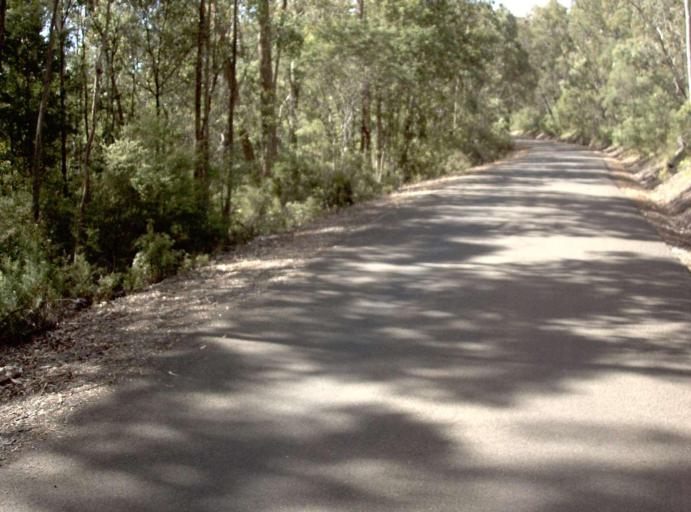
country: AU
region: Victoria
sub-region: East Gippsland
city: Lakes Entrance
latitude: -37.4634
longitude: 148.1224
